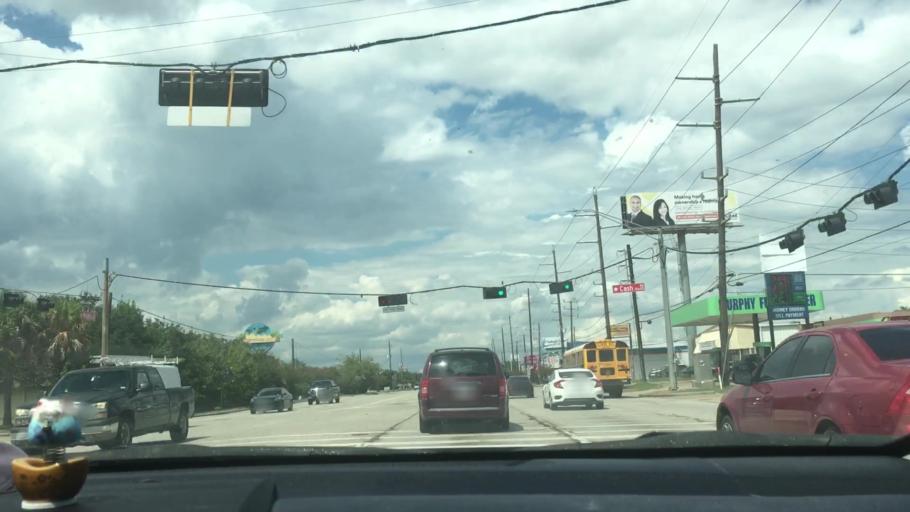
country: US
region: Texas
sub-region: Fort Bend County
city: Stafford
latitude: 29.6268
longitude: -95.5667
